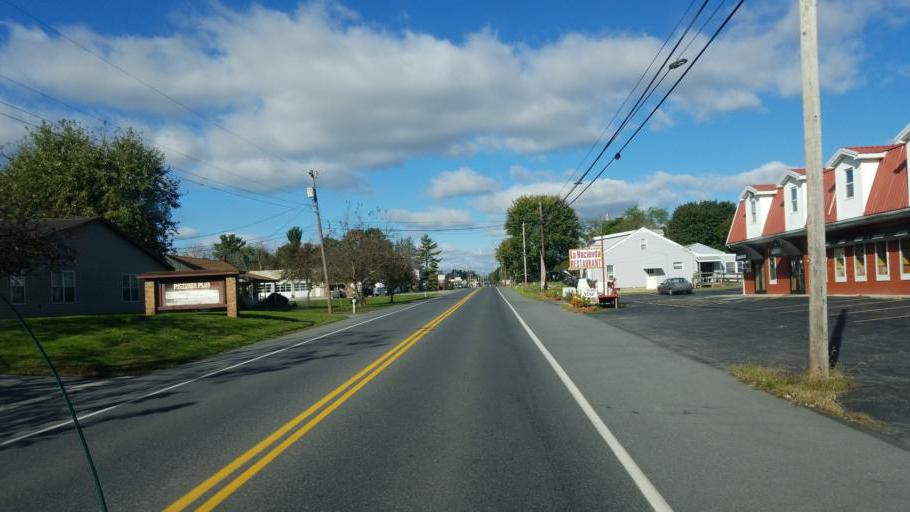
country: US
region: Pennsylvania
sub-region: Franklin County
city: Waynesboro
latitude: 39.7667
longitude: -77.6166
